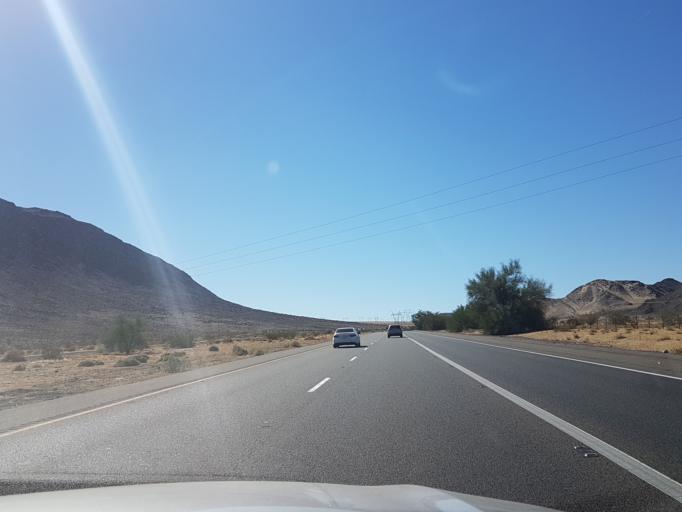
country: US
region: California
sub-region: San Bernardino County
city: Fort Irwin
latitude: 35.0920
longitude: -116.3097
